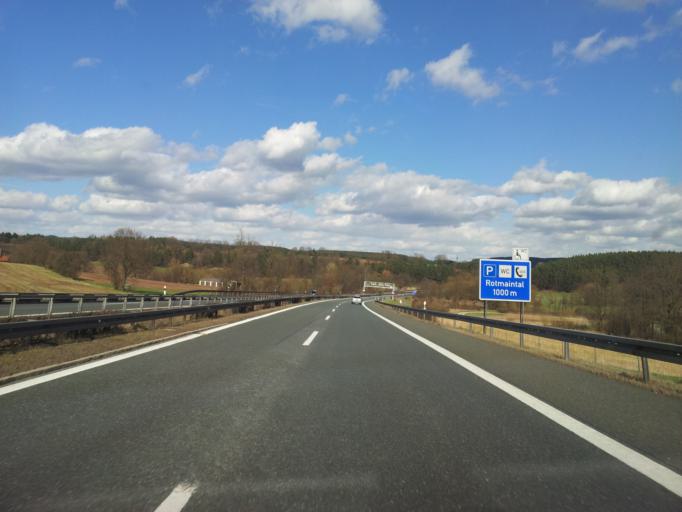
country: DE
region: Bavaria
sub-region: Upper Franconia
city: Neudrossenfeld
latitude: 50.0276
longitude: 11.4549
